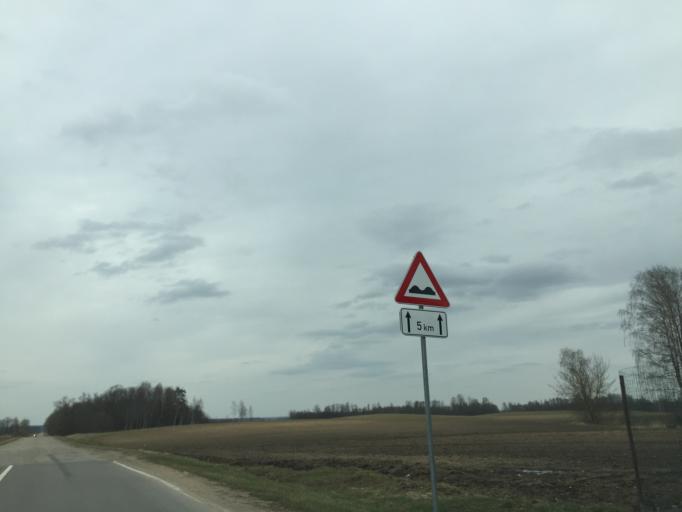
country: LV
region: Ilukste
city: Ilukste
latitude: 56.0108
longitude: 26.2698
